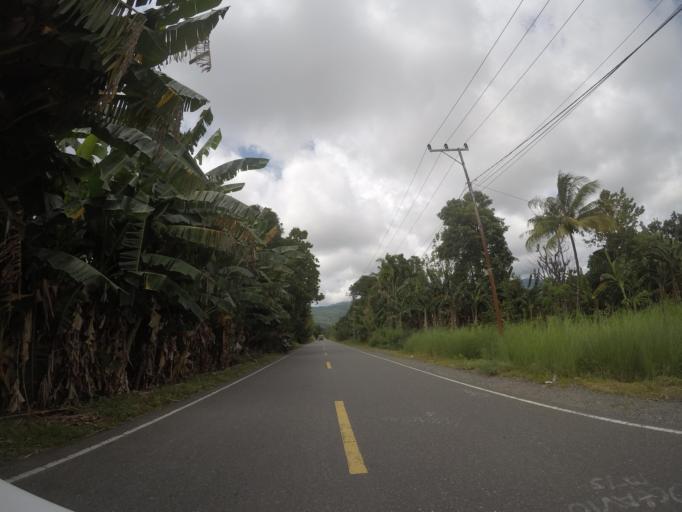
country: TL
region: Liquica
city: Maubara
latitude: -8.7350
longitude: 125.1364
